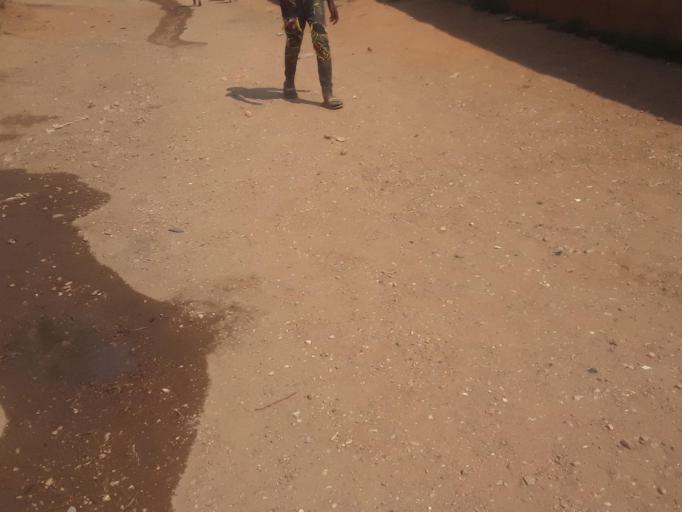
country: ZM
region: Lusaka
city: Lusaka
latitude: -15.3594
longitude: 28.3032
